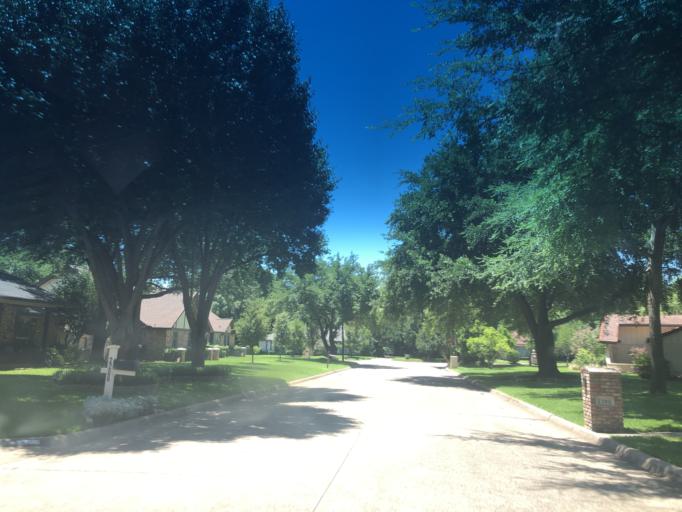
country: US
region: Texas
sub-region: Dallas County
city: Grand Prairie
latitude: 32.7738
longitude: -97.0408
